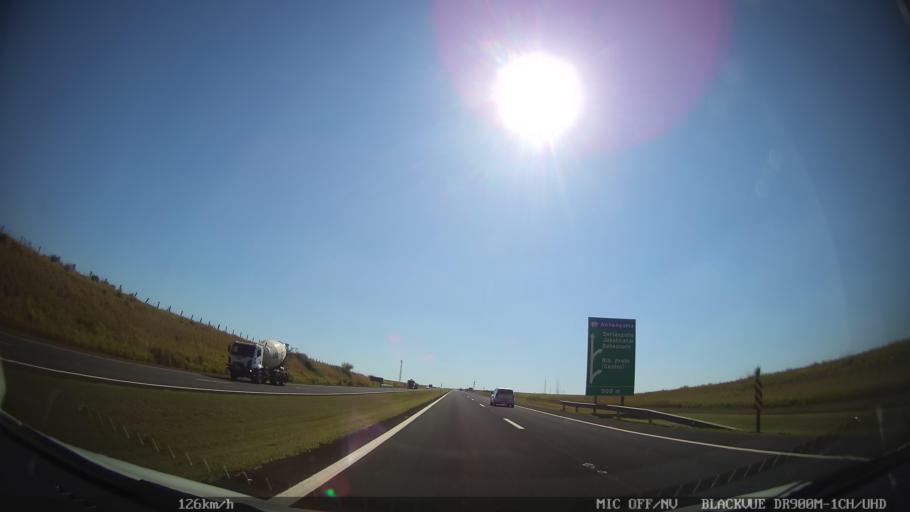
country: BR
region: Sao Paulo
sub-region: Ribeirao Preto
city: Ribeirao Preto
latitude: -21.1736
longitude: -47.8966
